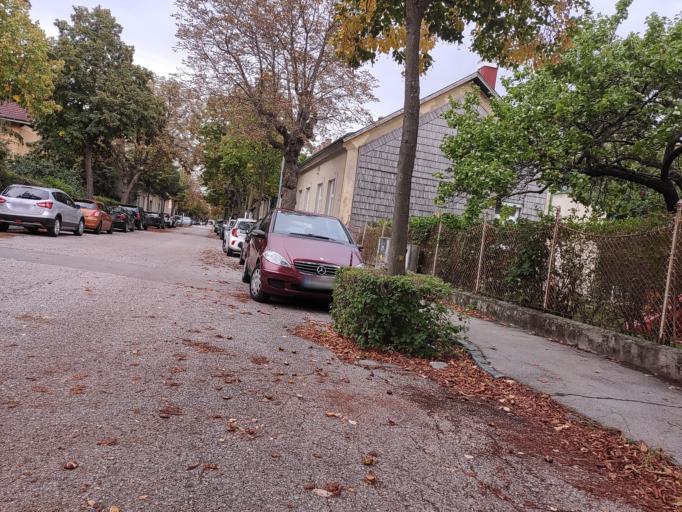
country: AT
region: Lower Austria
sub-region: Politischer Bezirk Baden
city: Baden
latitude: 48.0016
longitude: 16.2320
